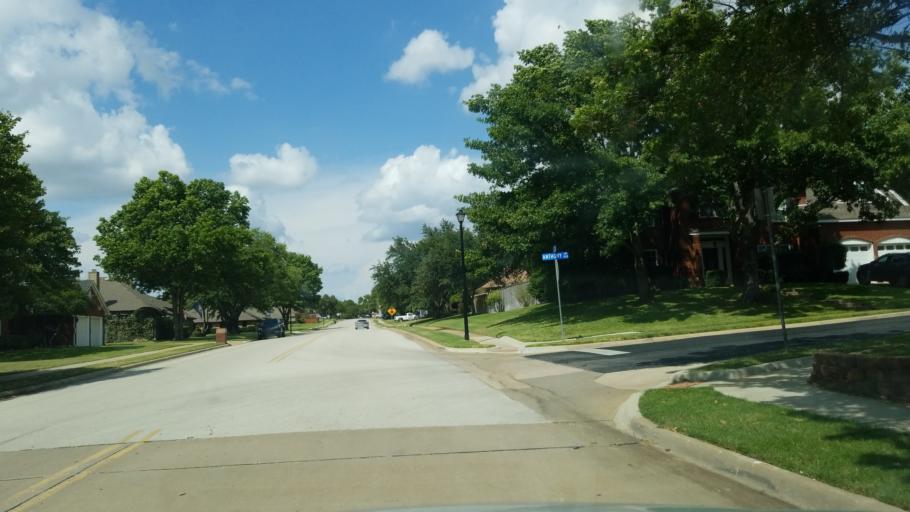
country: US
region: Texas
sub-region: Tarrant County
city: Euless
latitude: 32.8697
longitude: -97.0907
